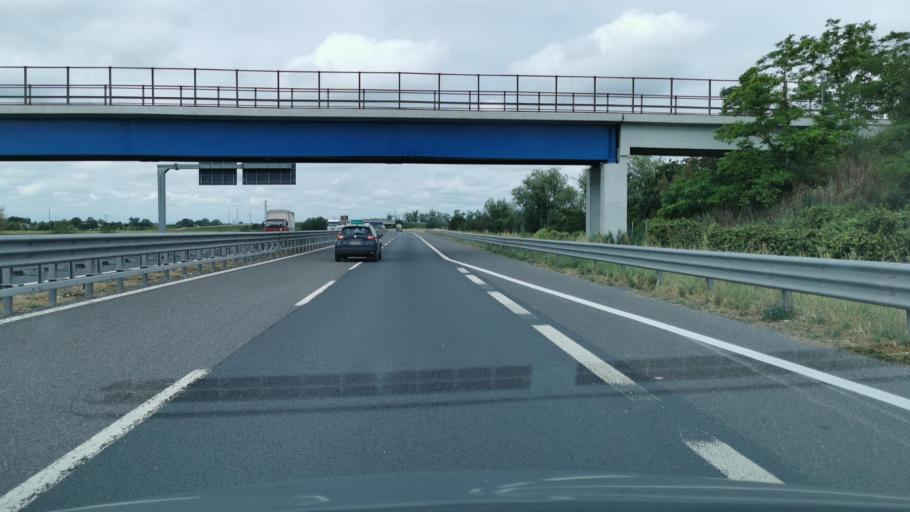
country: IT
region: Emilia-Romagna
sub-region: Provincia di Ravenna
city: Fornace Zarattini
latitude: 44.4144
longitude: 12.1200
